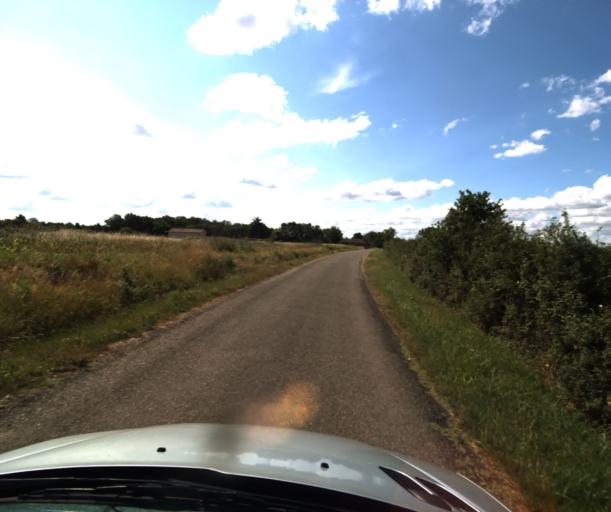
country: FR
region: Midi-Pyrenees
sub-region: Departement du Tarn-et-Garonne
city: Finhan
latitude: 43.8972
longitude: 1.2723
